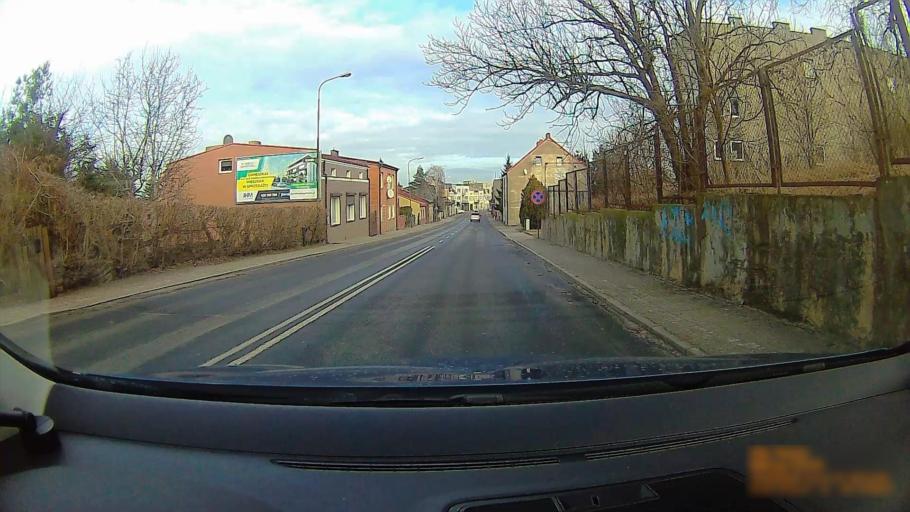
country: PL
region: Greater Poland Voivodeship
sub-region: Konin
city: Konin
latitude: 52.2039
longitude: 18.2498
